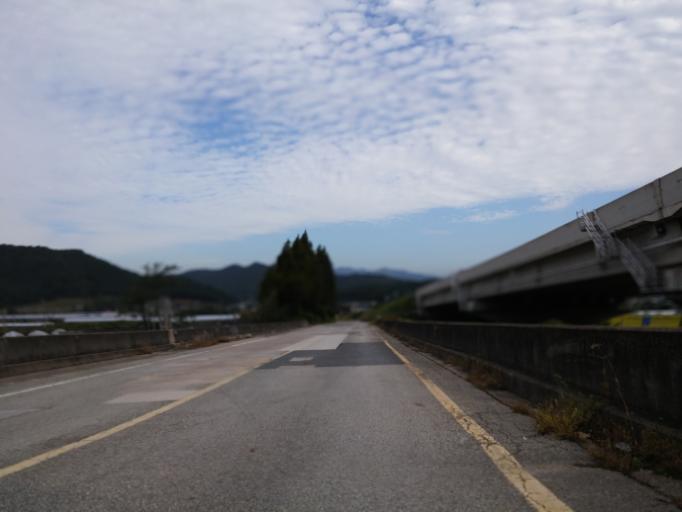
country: KR
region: Chungcheongnam-do
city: Yonmu
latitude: 36.1623
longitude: 127.1990
